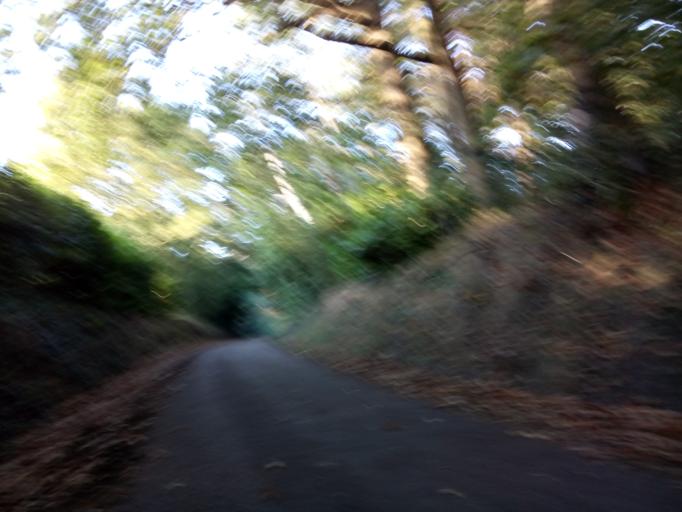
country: GB
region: England
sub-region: Suffolk
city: Bramford
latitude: 52.0379
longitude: 1.1060
